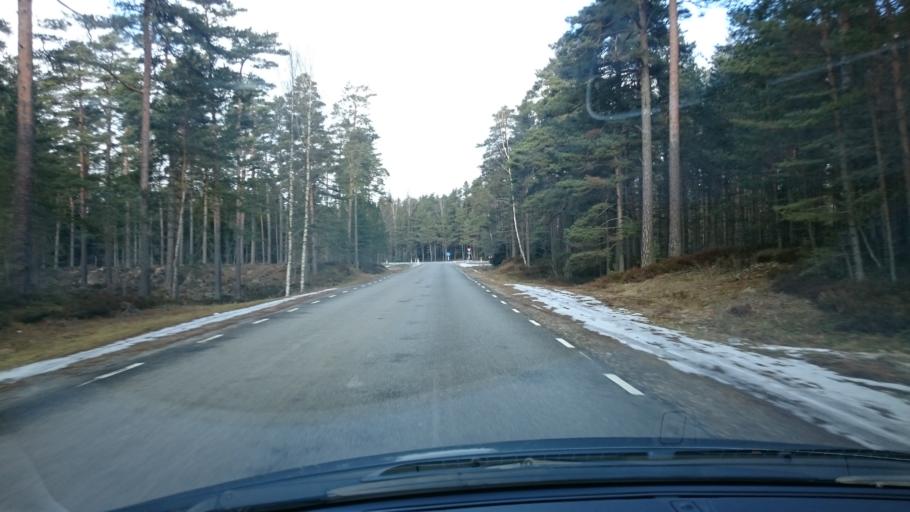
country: EE
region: Harju
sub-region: Keila linn
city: Keila
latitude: 59.3914
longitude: 24.2945
